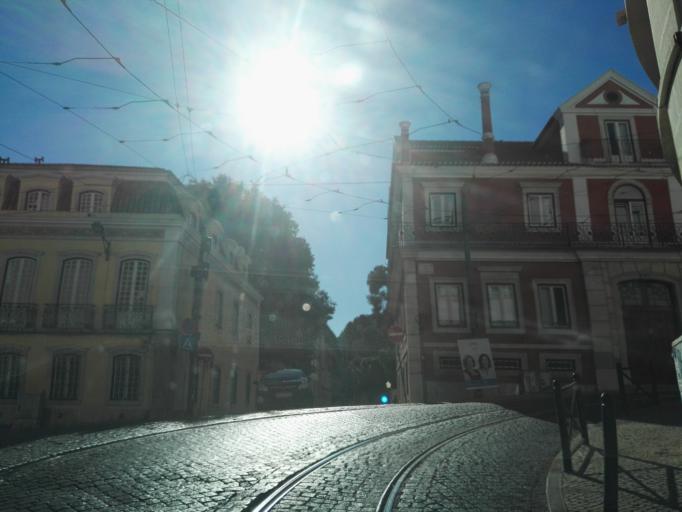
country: PT
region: Setubal
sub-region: Almada
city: Cacilhas
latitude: 38.7071
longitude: -9.1610
